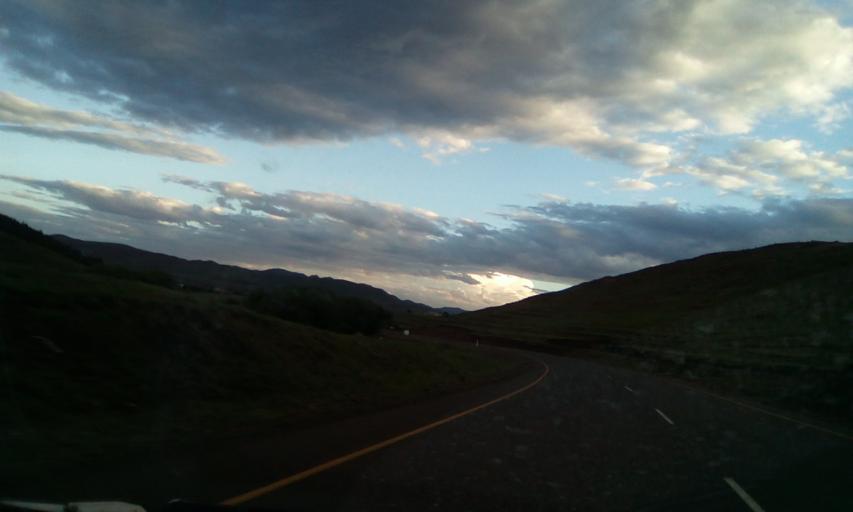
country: LS
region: Maseru
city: Nako
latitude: -29.8235
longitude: 28.0338
